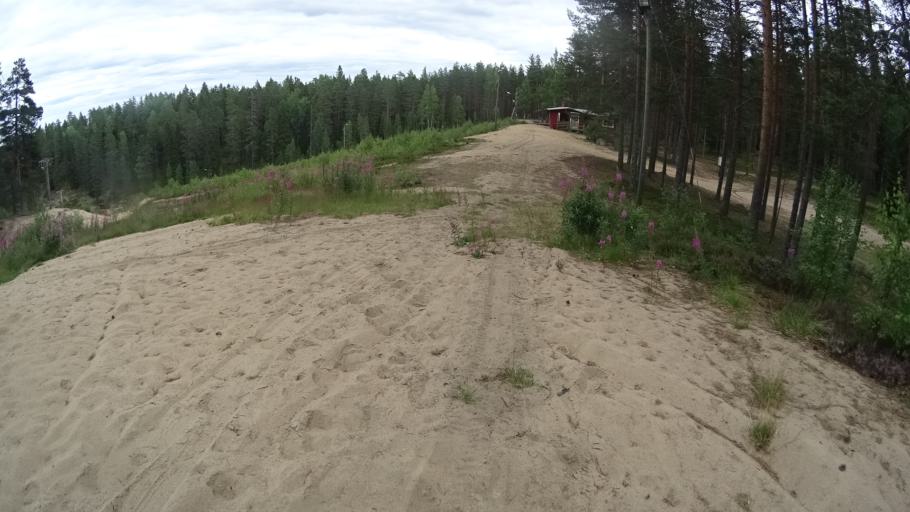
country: FI
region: Satakunta
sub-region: Pohjois-Satakunta
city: Jaemijaervi
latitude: 61.7717
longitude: 22.7486
